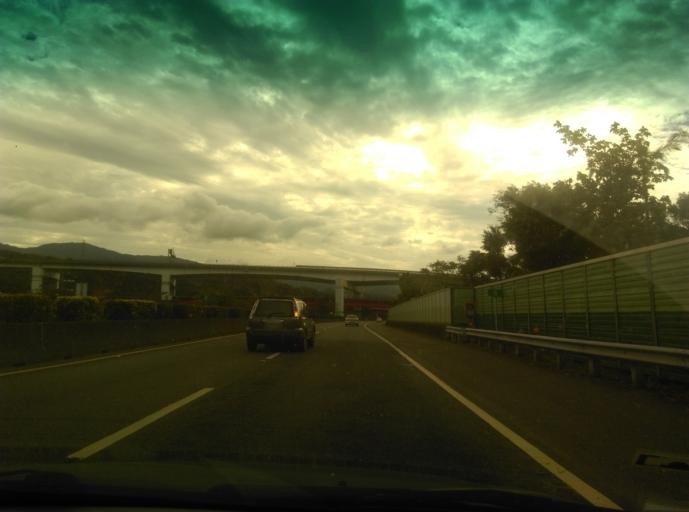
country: TW
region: Taiwan
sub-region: Keelung
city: Keelung
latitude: 25.1076
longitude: 121.7251
